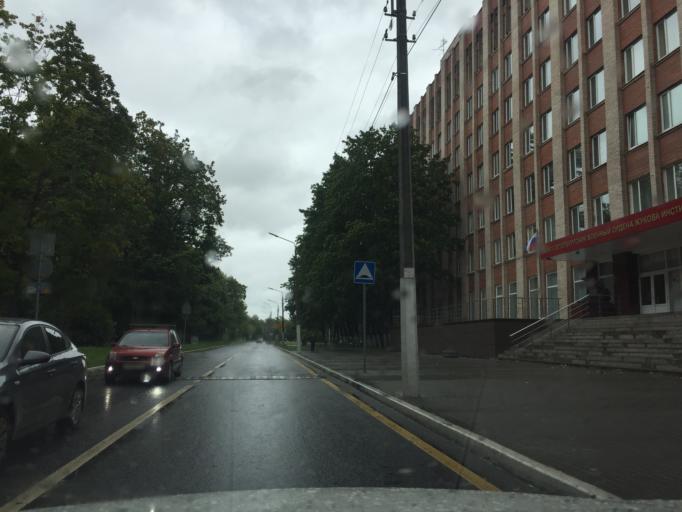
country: RU
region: St.-Petersburg
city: Sosnovaya Polyana
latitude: 59.8451
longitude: 30.1379
